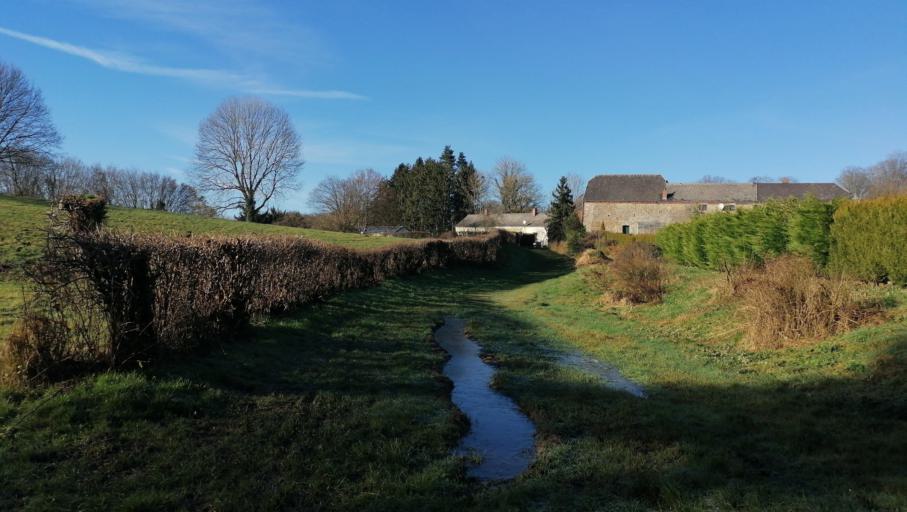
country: FR
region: Nord-Pas-de-Calais
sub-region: Departement du Nord
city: Recquignies
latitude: 50.2041
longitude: 4.0705
